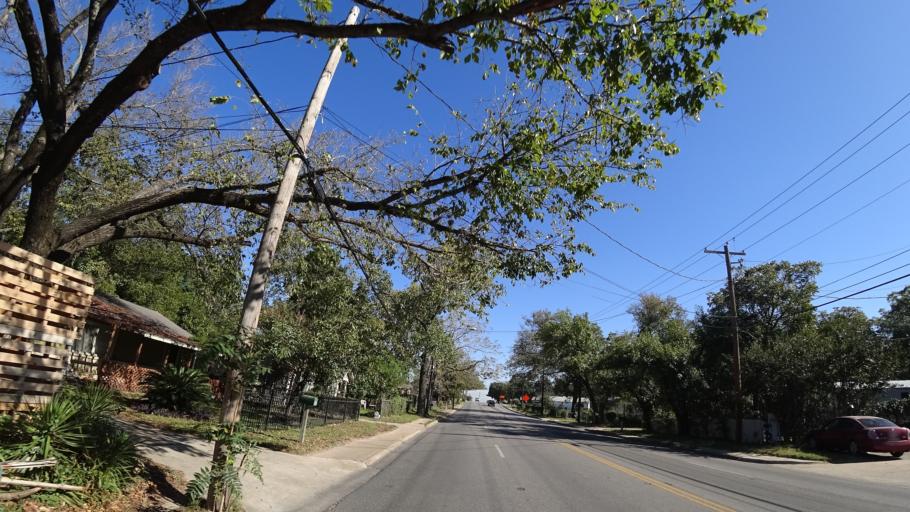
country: US
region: Texas
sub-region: Travis County
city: Austin
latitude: 30.2395
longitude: -97.6942
